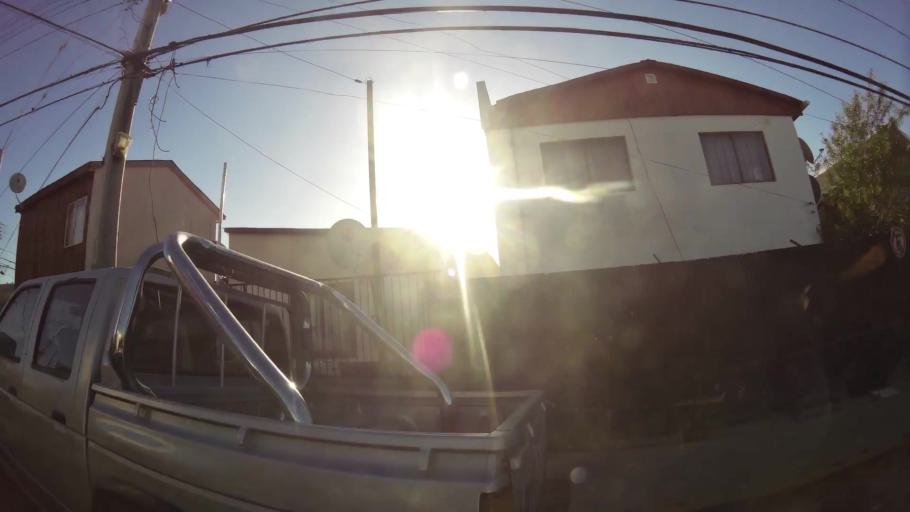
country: CL
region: Valparaiso
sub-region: Provincia de Valparaiso
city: Valparaiso
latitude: -33.0602
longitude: -71.6129
